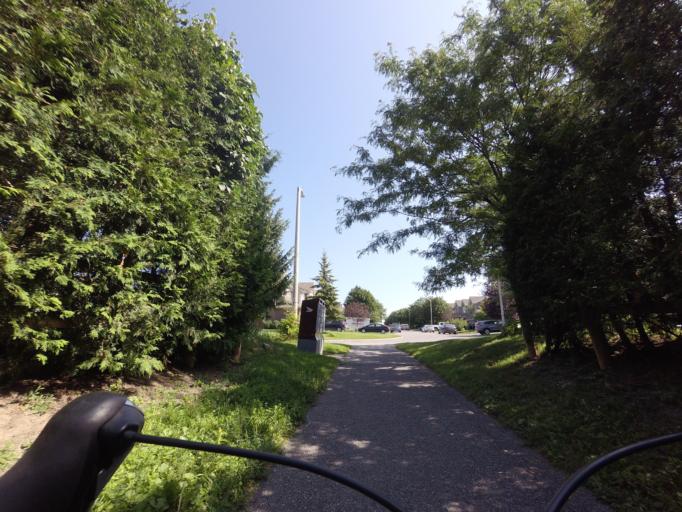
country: CA
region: Ontario
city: Bells Corners
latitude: 45.2800
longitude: -75.8515
